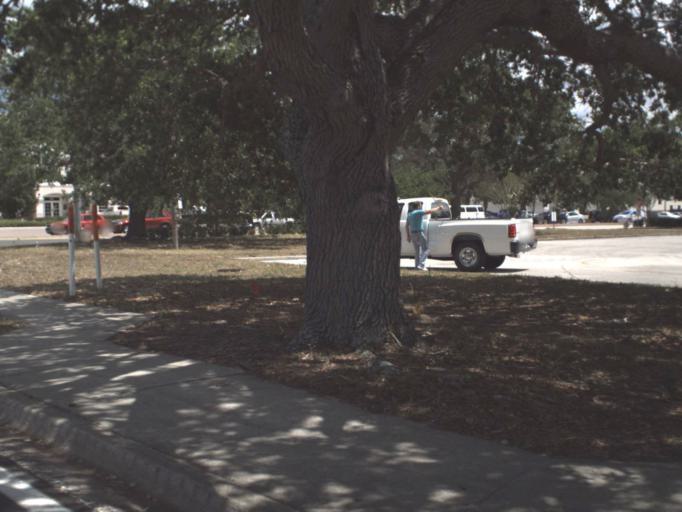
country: US
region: Florida
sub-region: Brevard County
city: Melbourne
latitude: 28.0933
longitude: -80.6224
